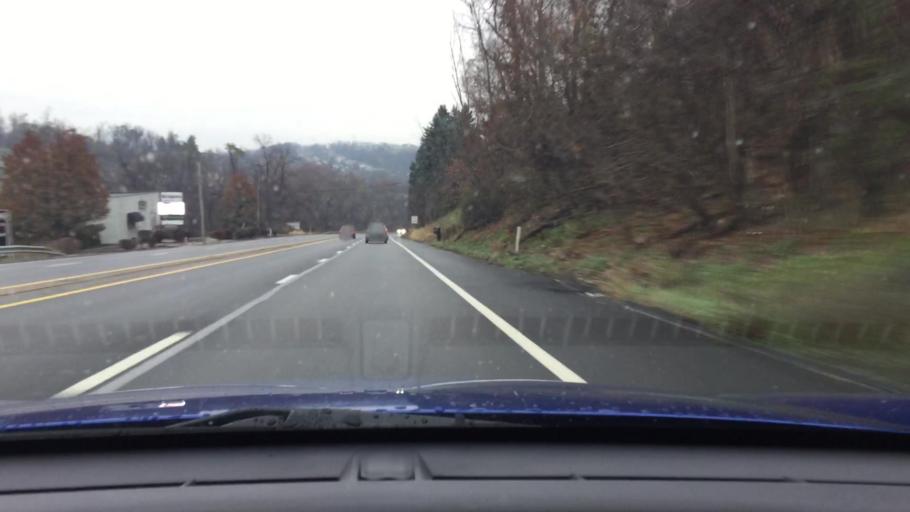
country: US
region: Pennsylvania
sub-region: Washington County
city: Canonsburg
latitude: 40.2475
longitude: -80.1739
